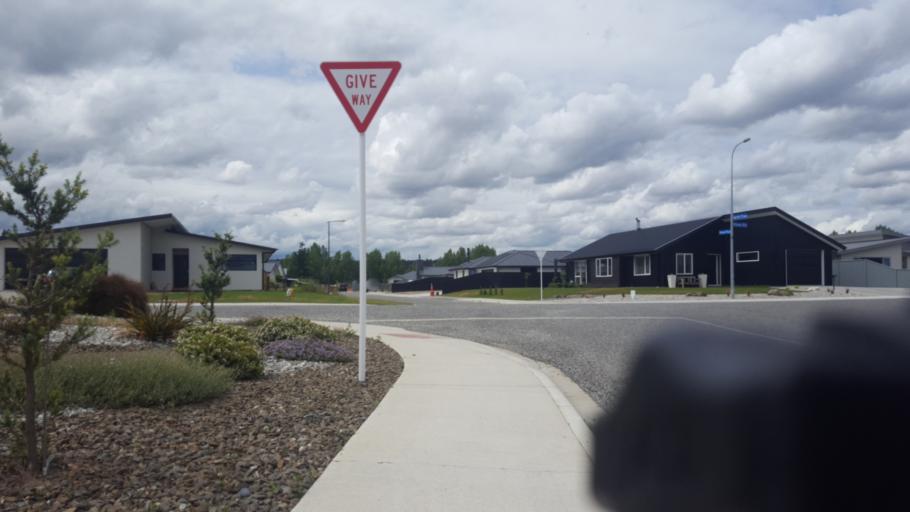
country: NZ
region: Otago
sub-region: Queenstown-Lakes District
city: Wanaka
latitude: -45.2433
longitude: 169.3745
